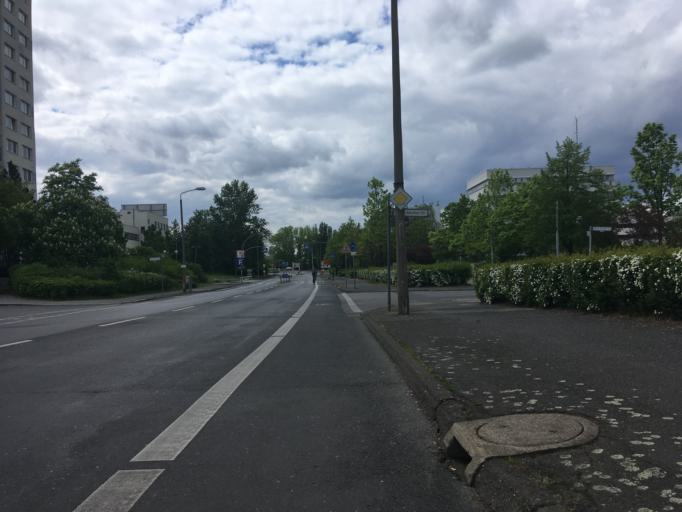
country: DE
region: Berlin
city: Biesdorf
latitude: 52.5345
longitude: 13.5405
